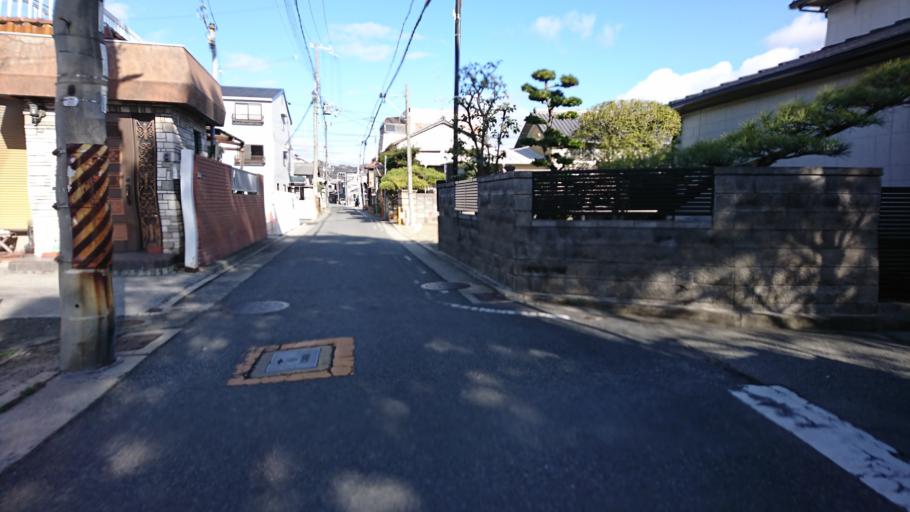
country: JP
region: Hyogo
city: Shirahamacho-usazakiminami
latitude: 34.7781
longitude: 134.7726
